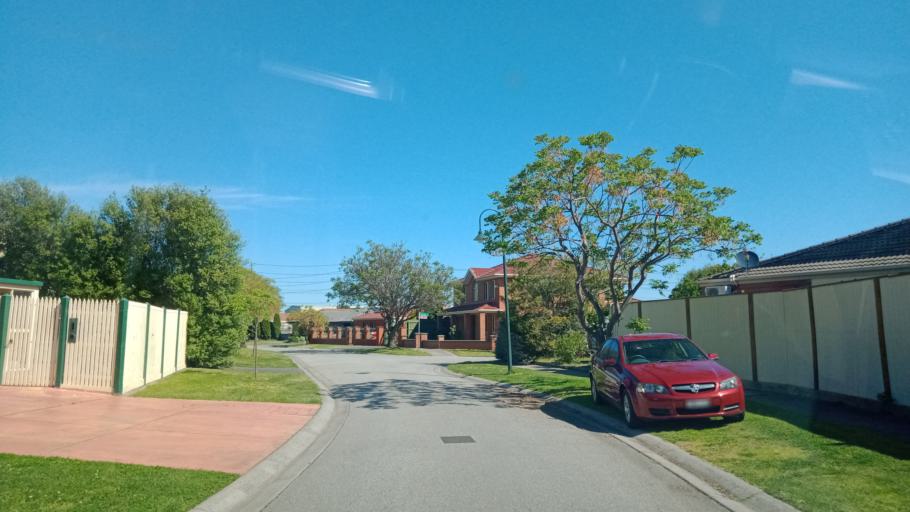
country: AU
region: Victoria
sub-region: Monash
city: Oakleigh South
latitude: -37.9365
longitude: 145.0727
